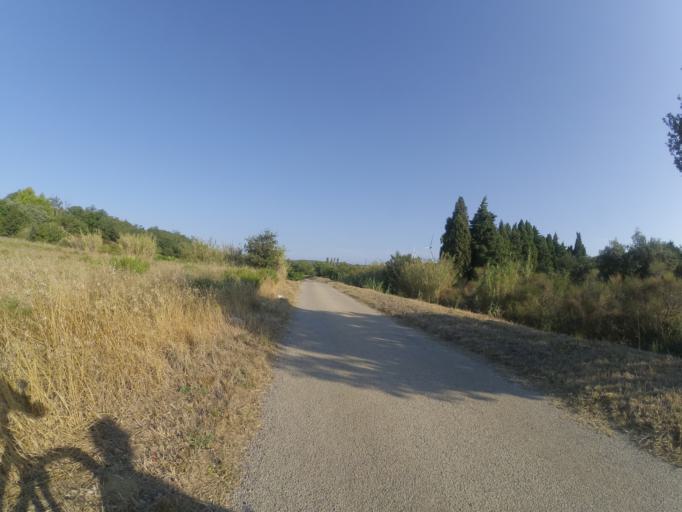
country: FR
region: Languedoc-Roussillon
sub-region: Departement des Pyrenees-Orientales
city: Pezilla-la-Riviere
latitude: 42.7088
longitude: 2.7718
